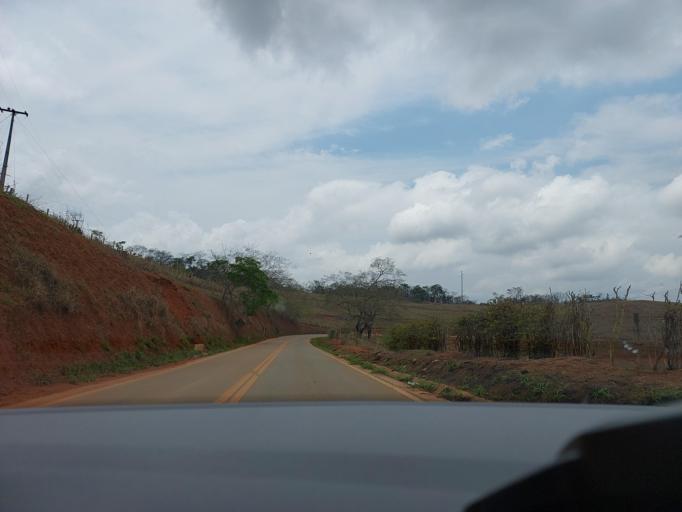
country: BR
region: Minas Gerais
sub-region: Ponte Nova
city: Ponte Nova
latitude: -20.3894
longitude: -42.8712
